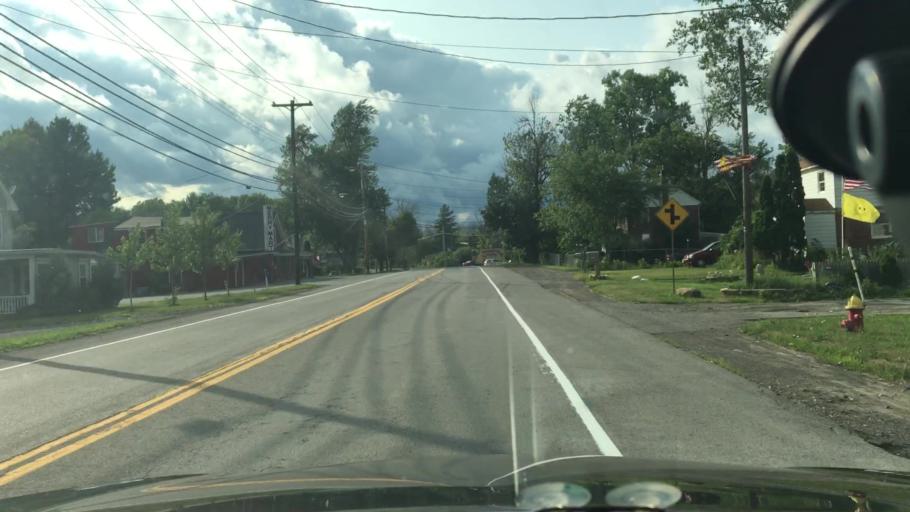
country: US
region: New York
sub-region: Erie County
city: Elma Center
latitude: 42.8215
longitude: -78.6811
